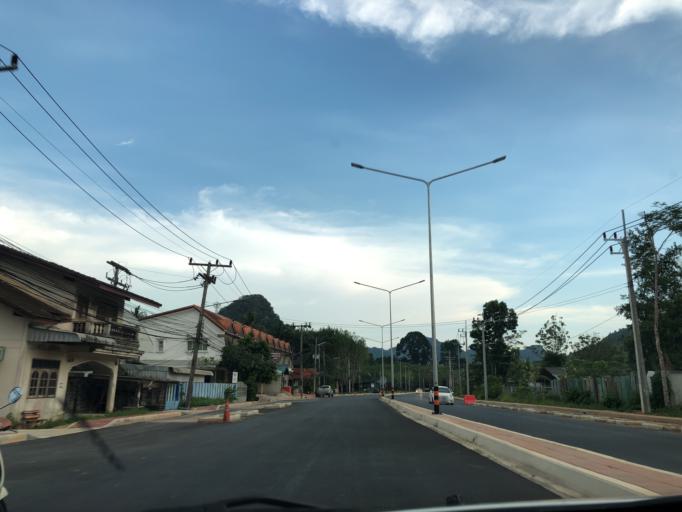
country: TH
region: Phangnga
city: Ban Ao Nang
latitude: 8.0598
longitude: 98.8404
